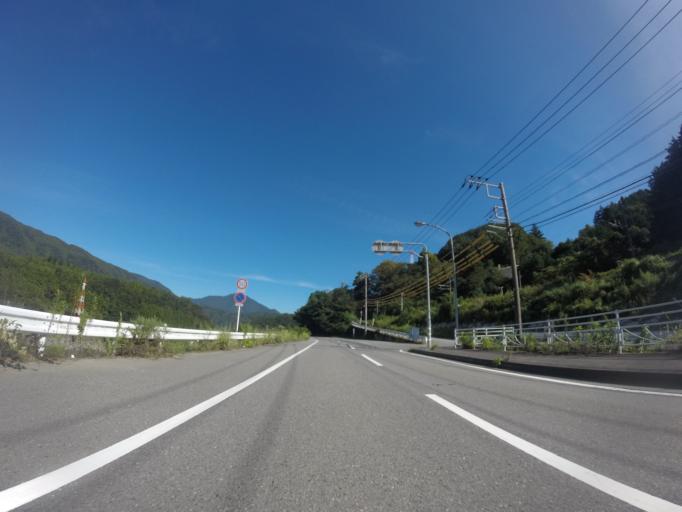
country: JP
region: Shizuoka
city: Fujinomiya
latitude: 35.3371
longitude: 138.4496
